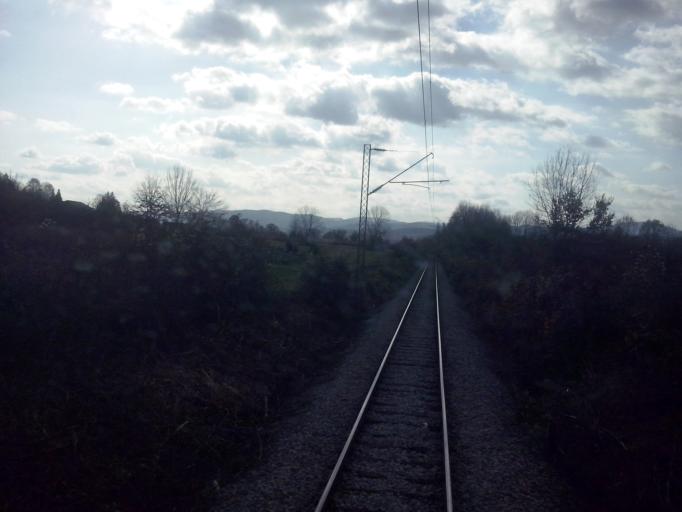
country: RS
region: Central Serbia
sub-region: Zlatiborski Okrug
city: Pozega
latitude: 43.8831
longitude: 19.9999
